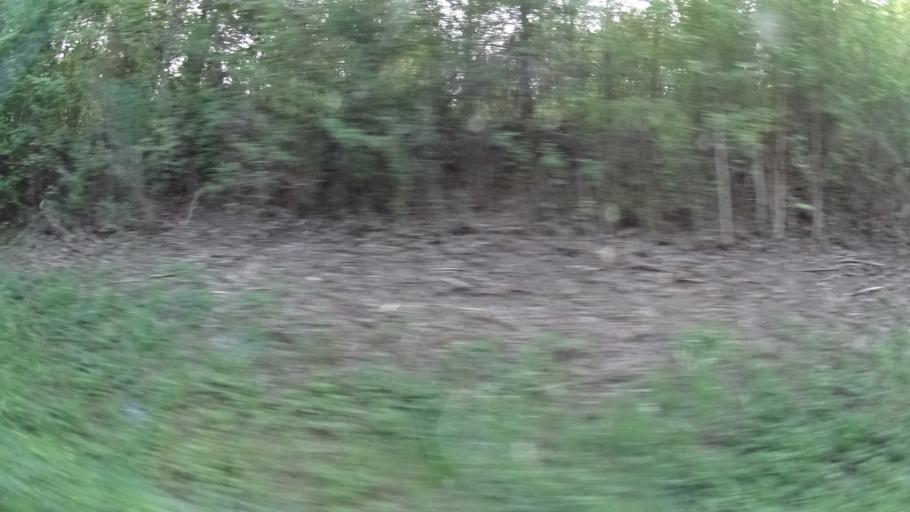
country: DE
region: Baden-Wuerttemberg
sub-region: Tuebingen Region
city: Haigerloch
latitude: 48.3881
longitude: 8.7898
